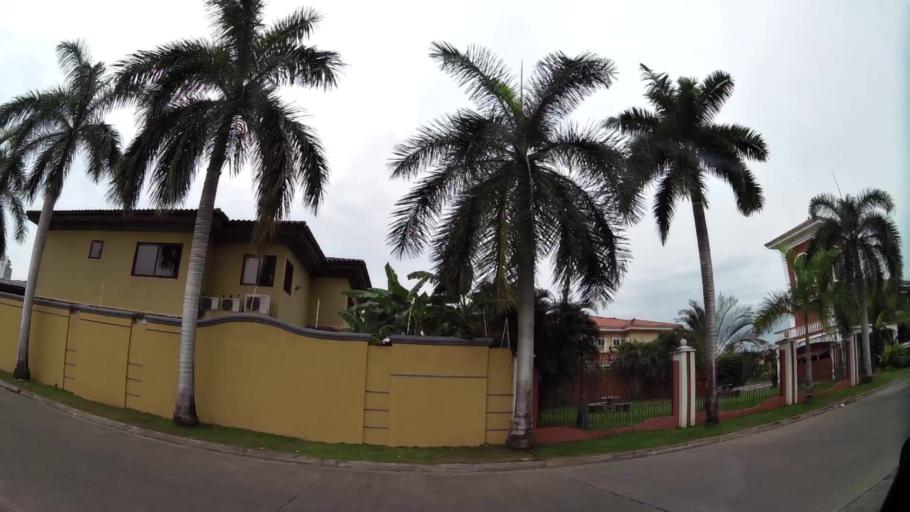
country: PA
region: Panama
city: San Miguelito
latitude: 9.0209
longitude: -79.4595
